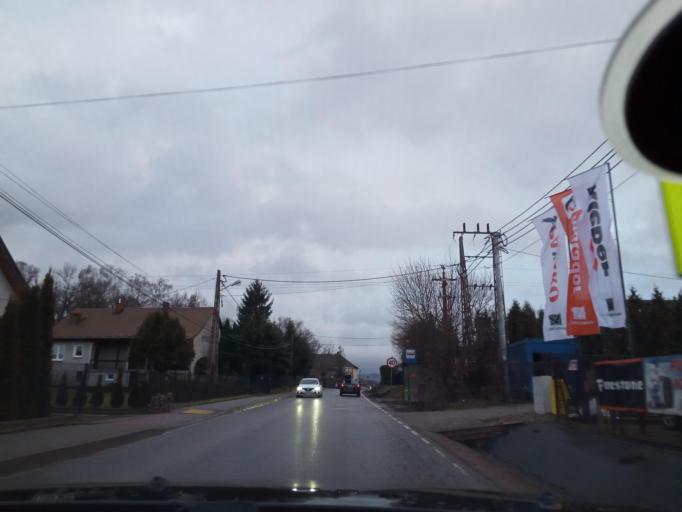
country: PL
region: Lesser Poland Voivodeship
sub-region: Powiat wielicki
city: Kokotow
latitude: 50.0119
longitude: 20.0841
